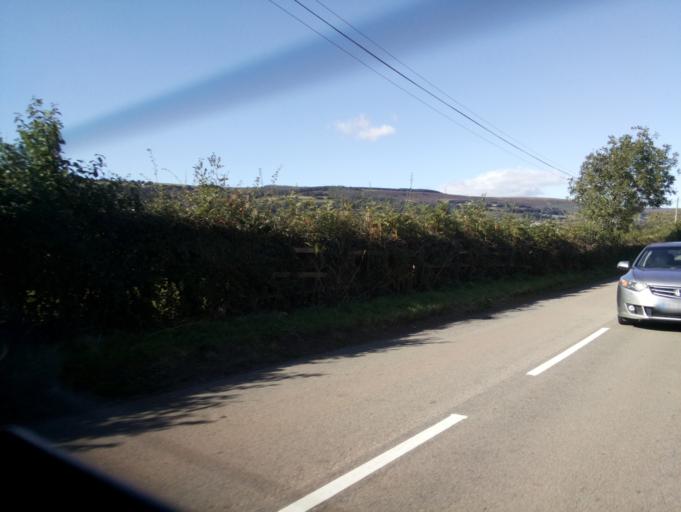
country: GB
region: Wales
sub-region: Torfaen County Borough
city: Cwmbran
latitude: 51.6224
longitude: -3.0523
